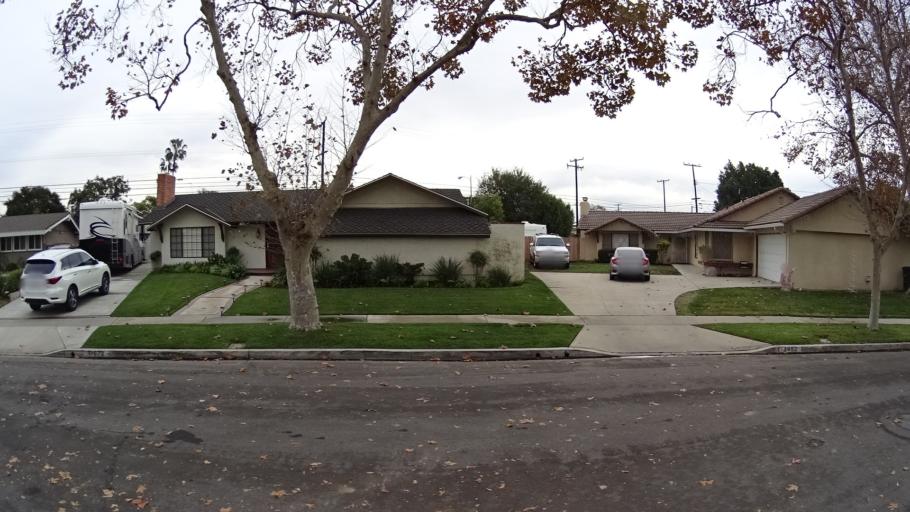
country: US
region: California
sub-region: Orange County
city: Los Alamitos
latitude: 33.7933
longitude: -118.0726
